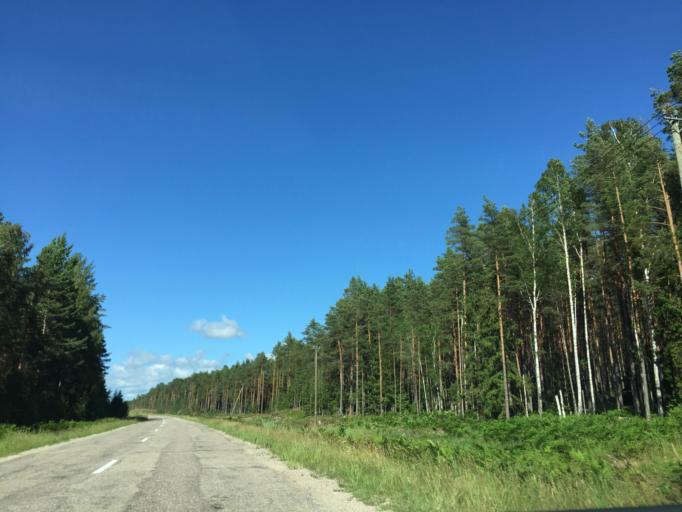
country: LV
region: Ventspils
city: Ventspils
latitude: 57.4748
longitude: 21.6648
